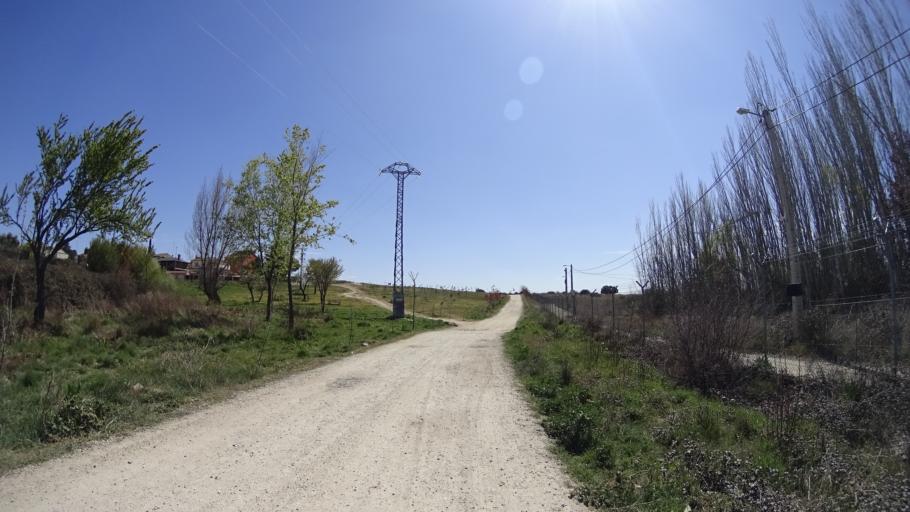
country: ES
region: Madrid
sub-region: Provincia de Madrid
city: Colmenar Viejo
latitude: 40.6717
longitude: -3.7860
